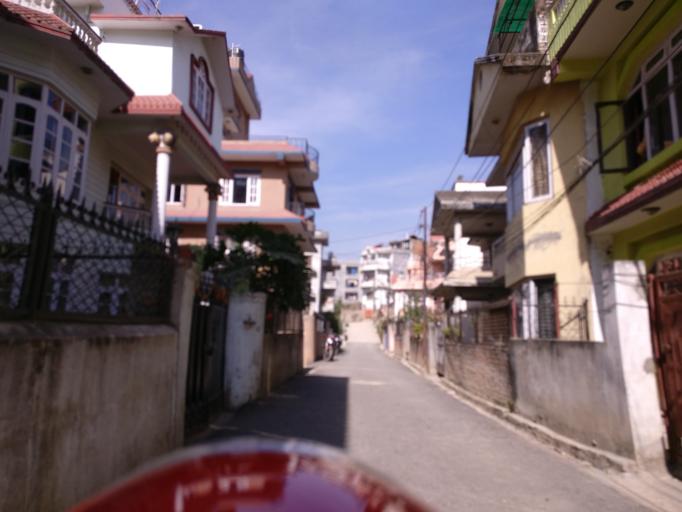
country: NP
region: Central Region
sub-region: Bagmati Zone
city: Patan
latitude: 27.6610
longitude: 85.3094
